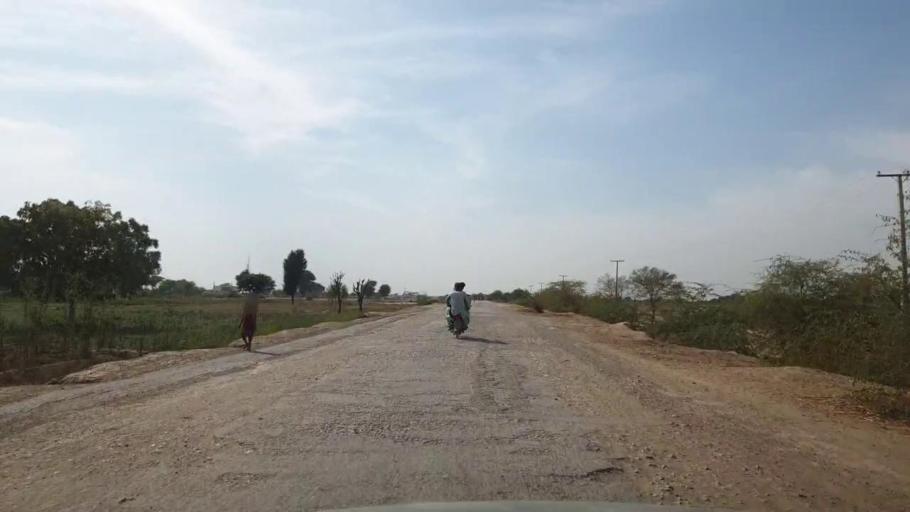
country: PK
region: Sindh
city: Kunri
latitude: 25.1689
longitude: 69.5238
